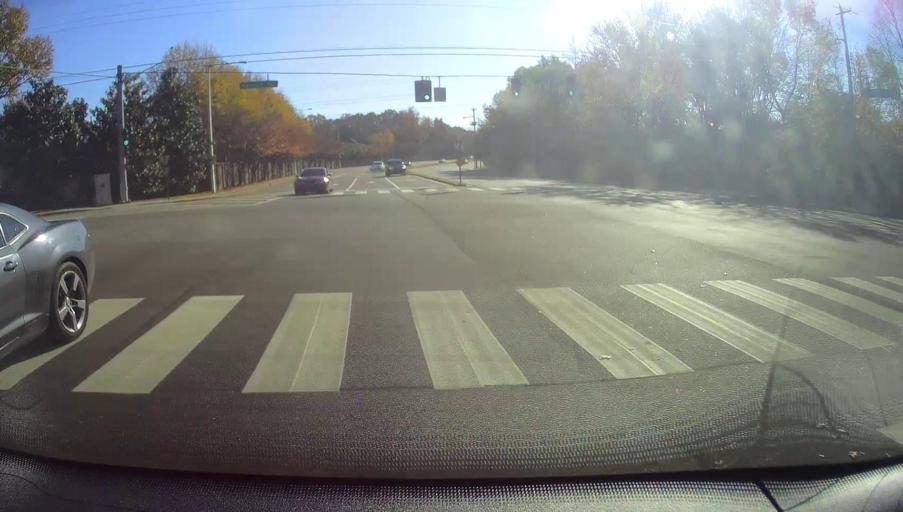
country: US
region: Tennessee
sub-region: Shelby County
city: Germantown
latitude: 35.0830
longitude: -89.8403
